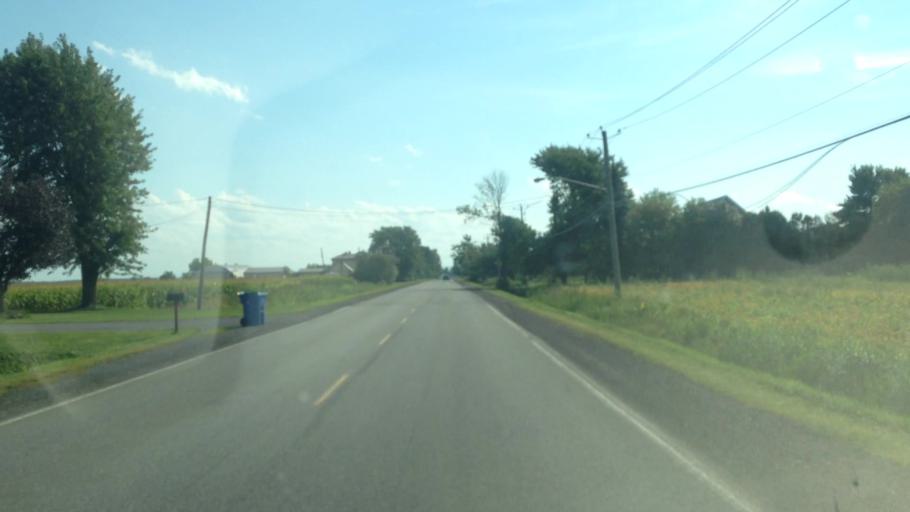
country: CA
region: Quebec
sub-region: Monteregie
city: Mercier
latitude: 45.2860
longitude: -73.6876
